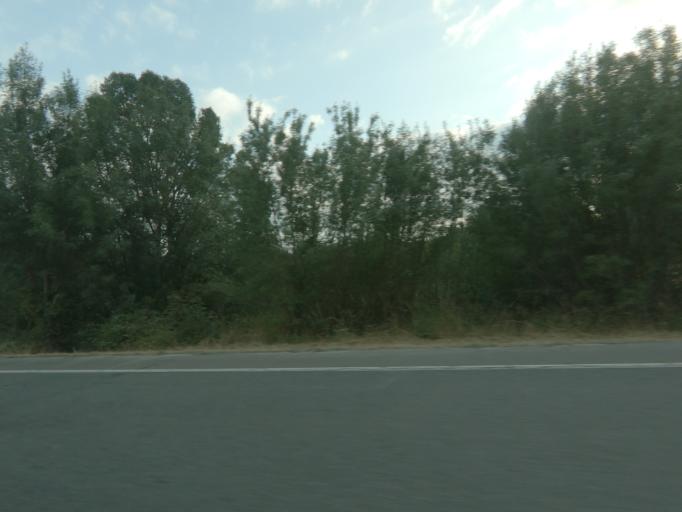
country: ES
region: Galicia
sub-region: Provincia de Ourense
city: Taboadela
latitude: 42.2804
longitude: -7.8379
